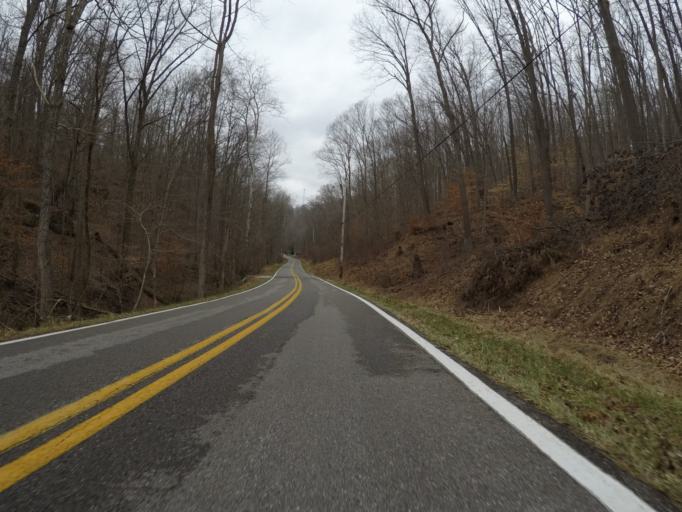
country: US
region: West Virginia
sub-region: Cabell County
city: Barboursville
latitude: 38.4572
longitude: -82.2669
